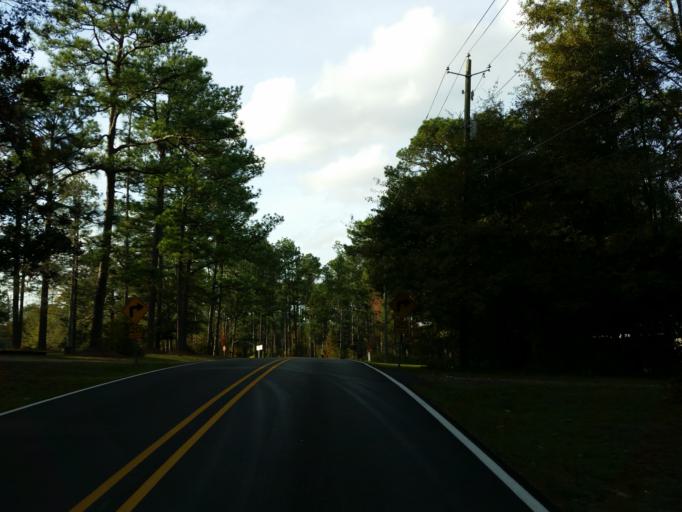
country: US
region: Mississippi
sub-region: Lamar County
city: West Hattiesburg
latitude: 31.2947
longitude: -89.3301
